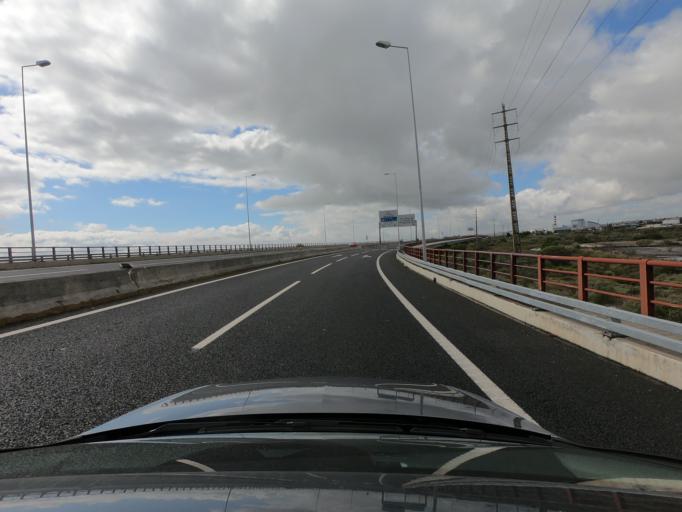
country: PT
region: Lisbon
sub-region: Loures
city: Santa Iria da Azoia
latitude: 38.8412
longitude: -9.0738
